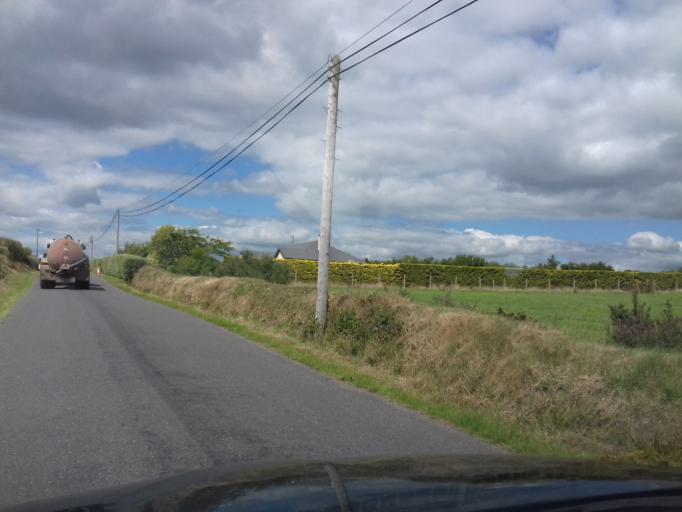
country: IE
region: Leinster
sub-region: Kilkenny
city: Mooncoin
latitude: 52.1732
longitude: -7.2810
